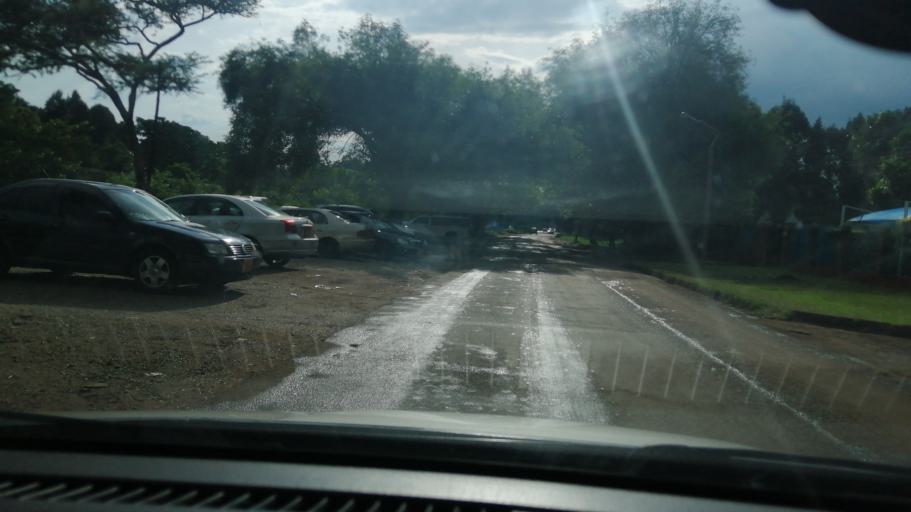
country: ZW
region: Harare
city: Harare
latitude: -17.8068
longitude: 31.0433
